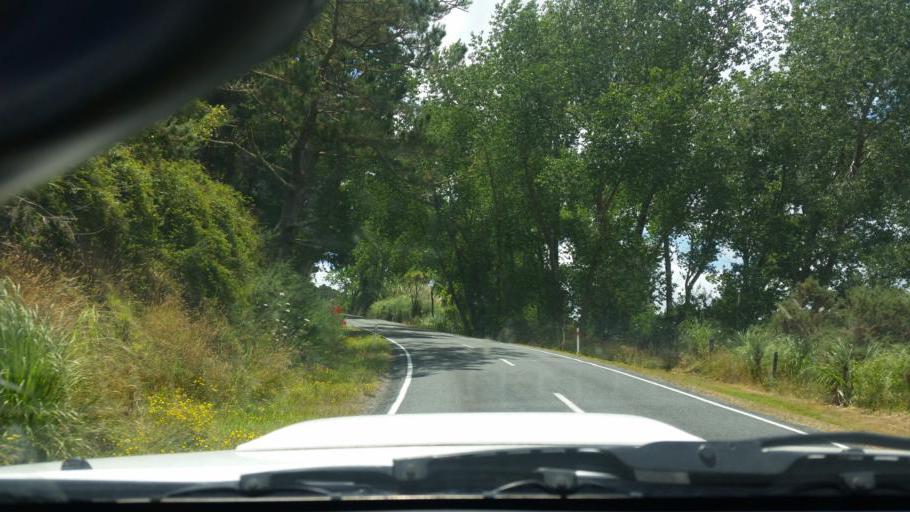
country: NZ
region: Northland
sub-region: Whangarei
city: Ruakaka
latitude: -36.0934
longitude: 174.2433
